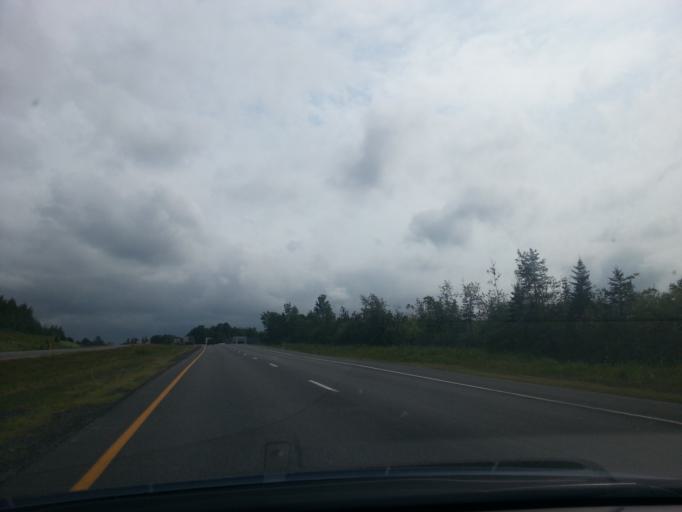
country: US
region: Maine
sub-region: Aroostook County
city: Houlton
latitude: 46.1352
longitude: -67.6099
